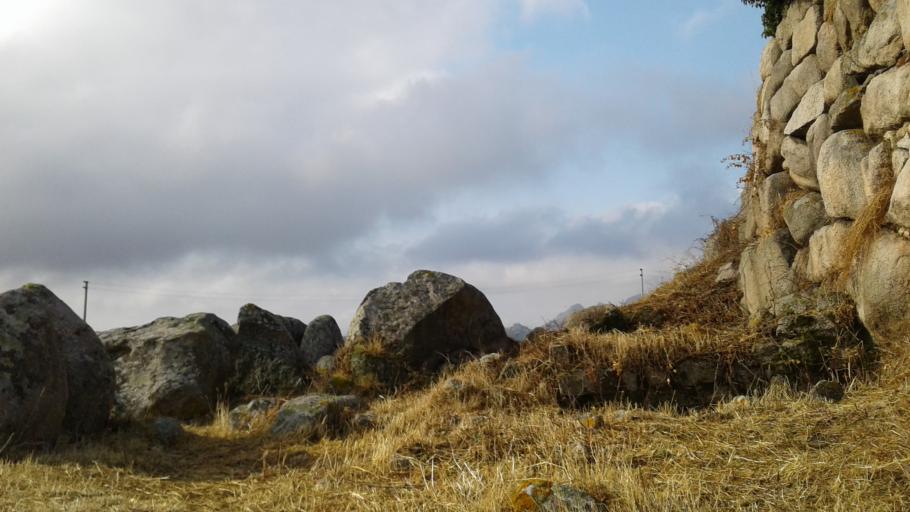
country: IT
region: Sardinia
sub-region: Provincia di Olbia-Tempio
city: Aggius
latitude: 40.9689
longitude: 9.0596
